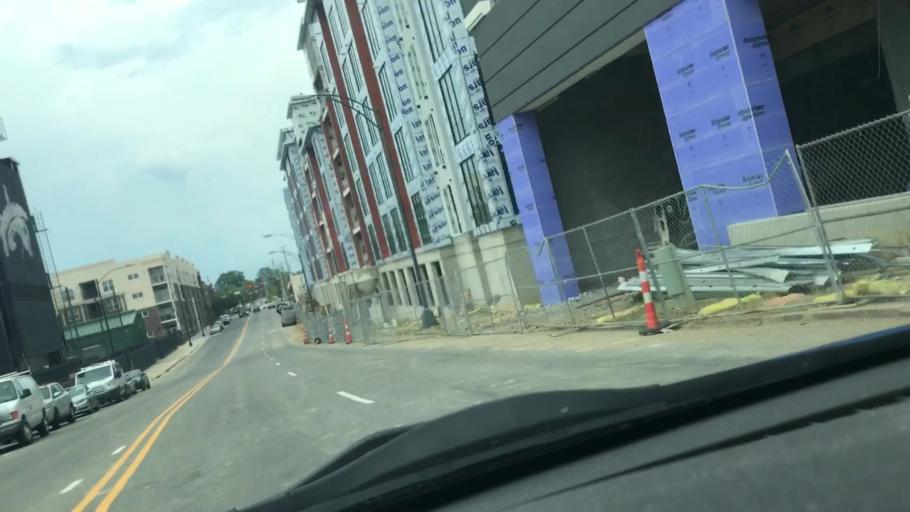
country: US
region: North Carolina
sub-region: Guilford County
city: Greensboro
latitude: 36.0747
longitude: -79.7937
